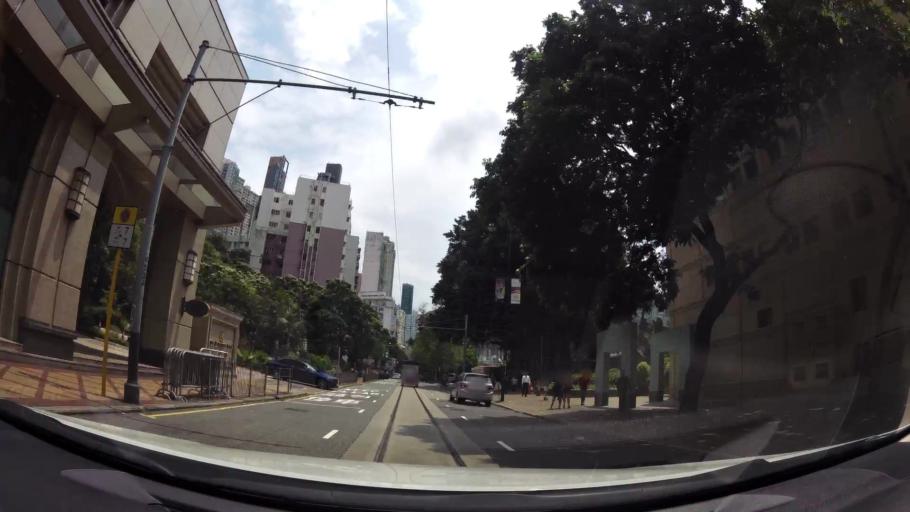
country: HK
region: Wanchai
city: Wan Chai
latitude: 22.2754
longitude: 114.1829
